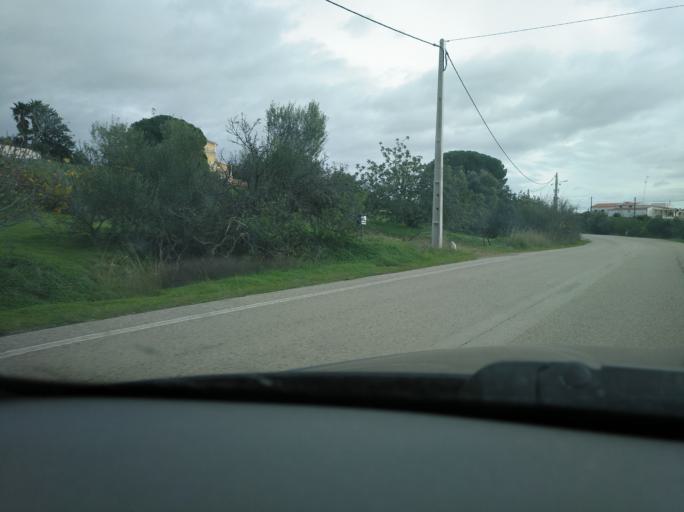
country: PT
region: Faro
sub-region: Castro Marim
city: Castro Marim
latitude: 37.2259
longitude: -7.4888
